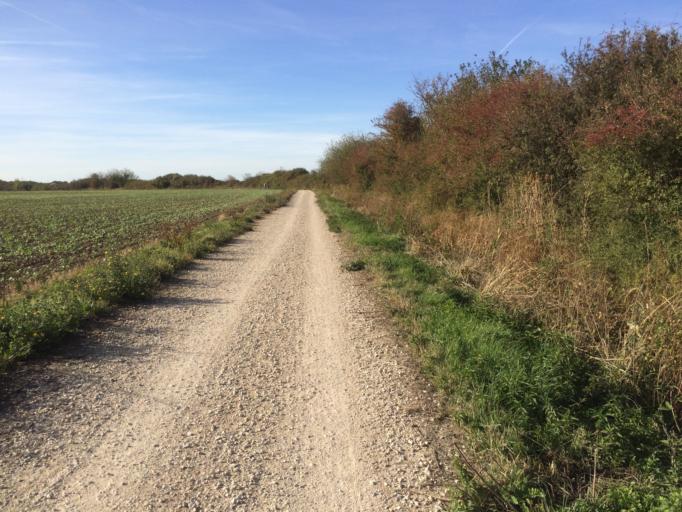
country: FR
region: Ile-de-France
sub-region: Departement de l'Essonne
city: Vauhallan
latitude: 48.7213
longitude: 2.2189
